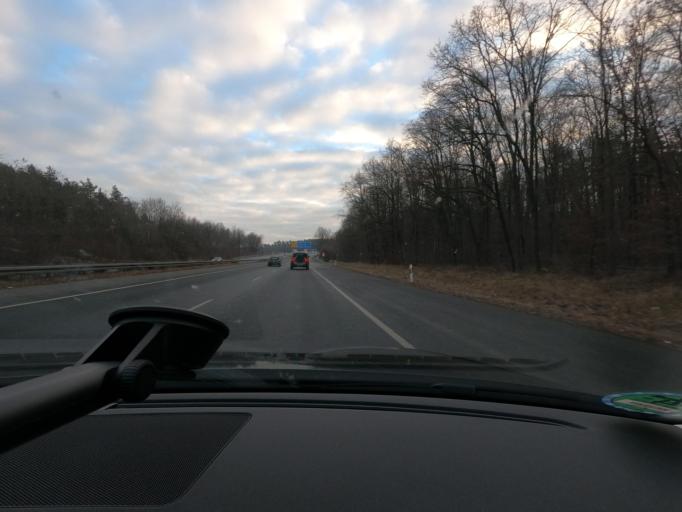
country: DE
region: Bavaria
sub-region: Regierungsbezirk Mittelfranken
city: Wendelstein
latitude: 49.3960
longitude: 11.1165
